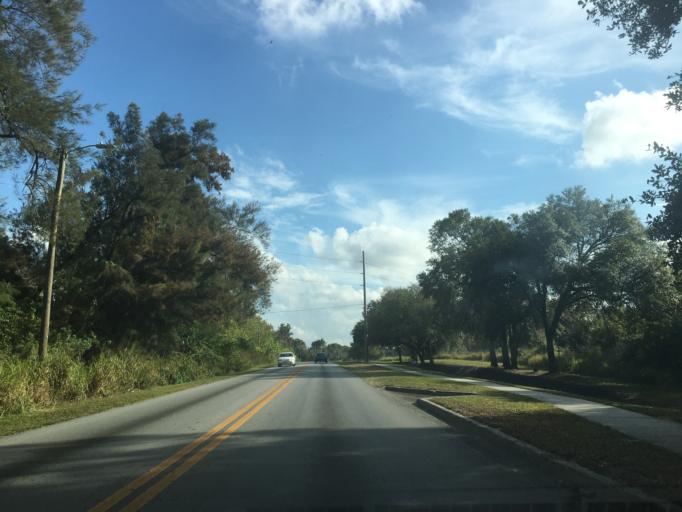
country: US
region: Florida
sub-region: Hillsborough County
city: Temple Terrace
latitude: 28.0212
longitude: -82.4344
